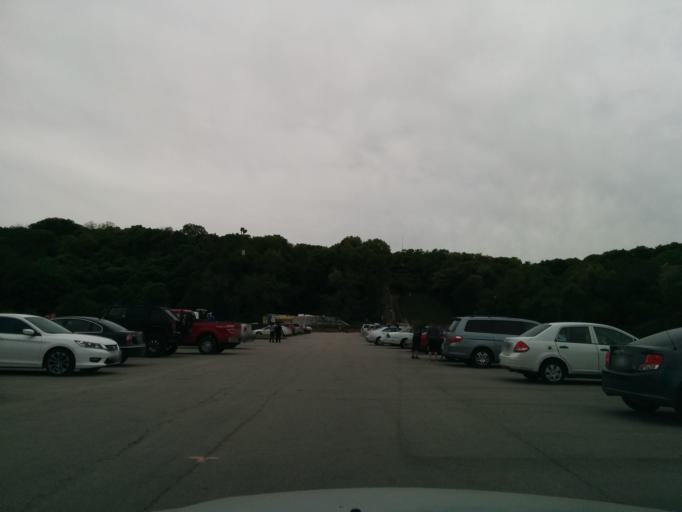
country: US
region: Illinois
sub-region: Cook County
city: Palos Park
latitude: 41.6820
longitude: -87.8621
